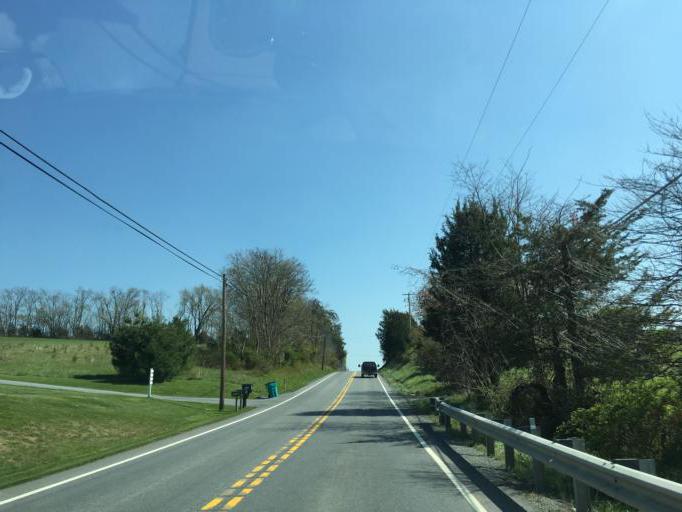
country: US
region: Maryland
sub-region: Frederick County
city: Woodsboro
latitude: 39.5116
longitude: -77.2816
